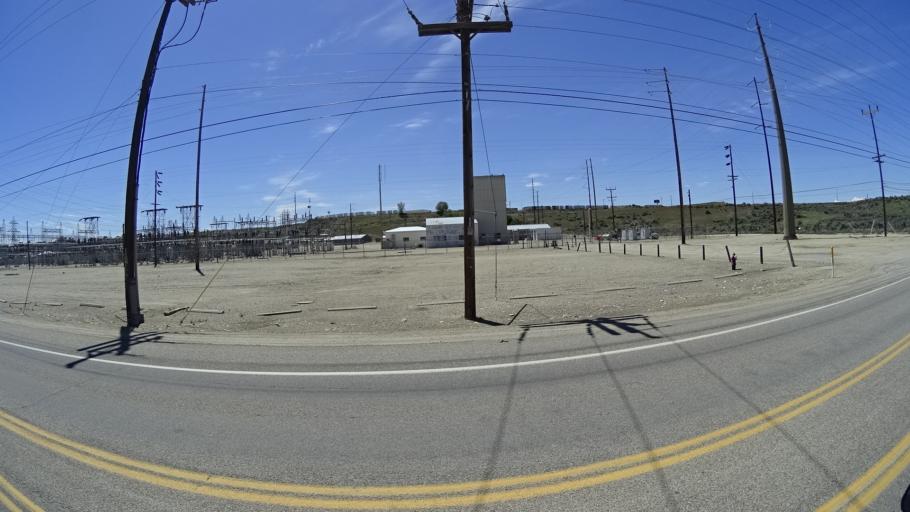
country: US
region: Idaho
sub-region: Ada County
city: Boise
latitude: 43.5607
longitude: -116.1599
